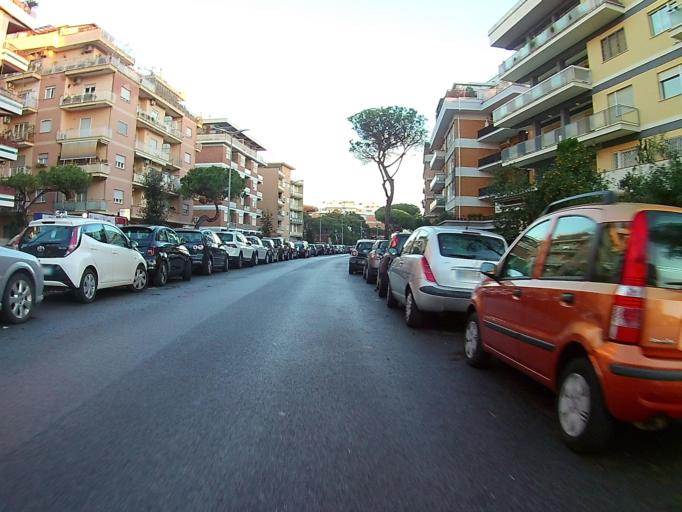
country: IT
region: Latium
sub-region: Citta metropolitana di Roma Capitale
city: Lido di Ostia
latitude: 41.7294
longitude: 12.2903
